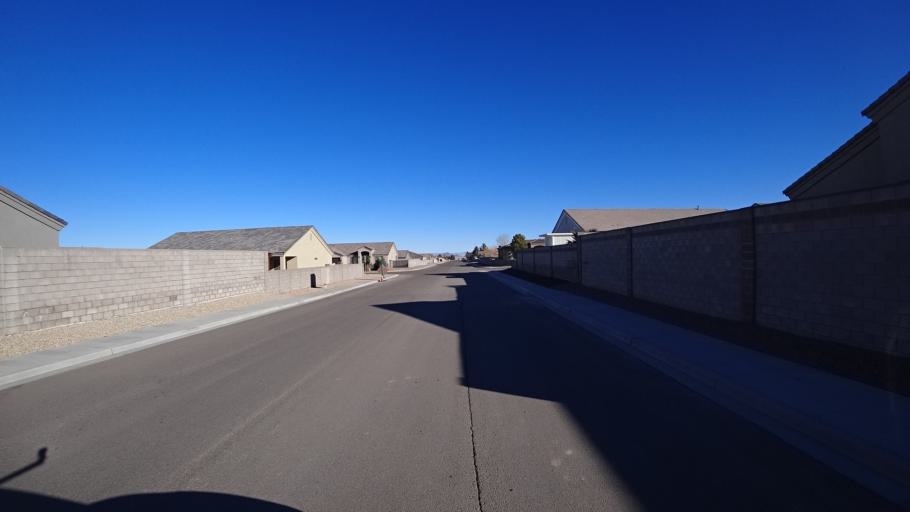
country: US
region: Arizona
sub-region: Mohave County
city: Kingman
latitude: 35.1916
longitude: -113.9982
